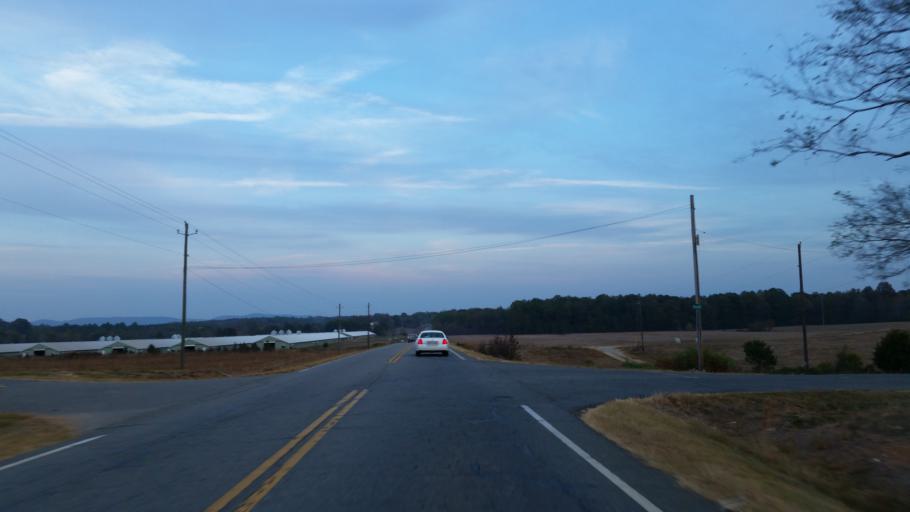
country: US
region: Georgia
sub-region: Murray County
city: Chatsworth
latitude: 34.6010
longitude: -84.7728
